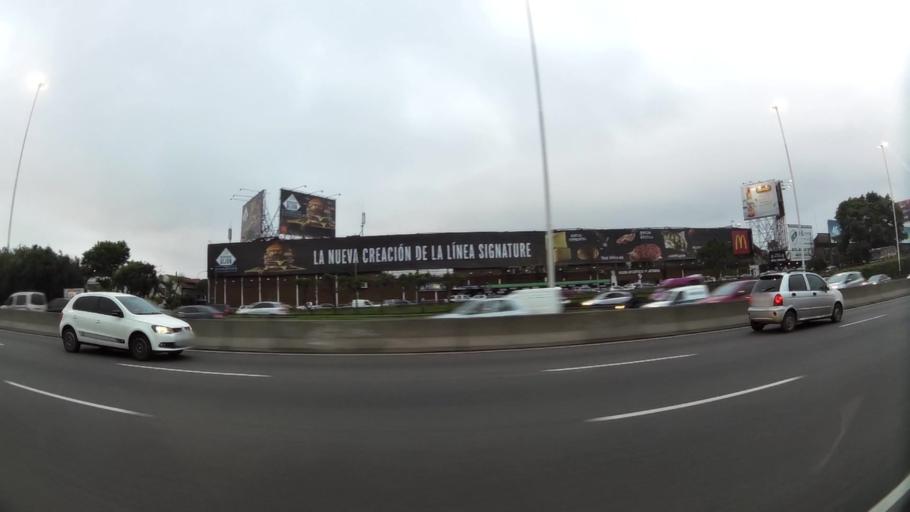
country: AR
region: Buenos Aires
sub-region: Partido de Vicente Lopez
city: Olivos
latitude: -34.5420
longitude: -58.4821
